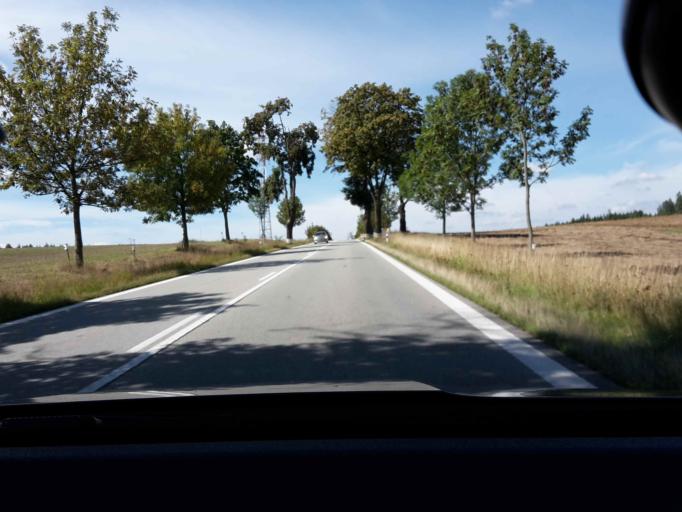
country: CZ
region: Jihocesky
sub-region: Okres Jindrichuv Hradec
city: Jindrichuv Hradec
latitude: 49.1620
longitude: 14.9413
